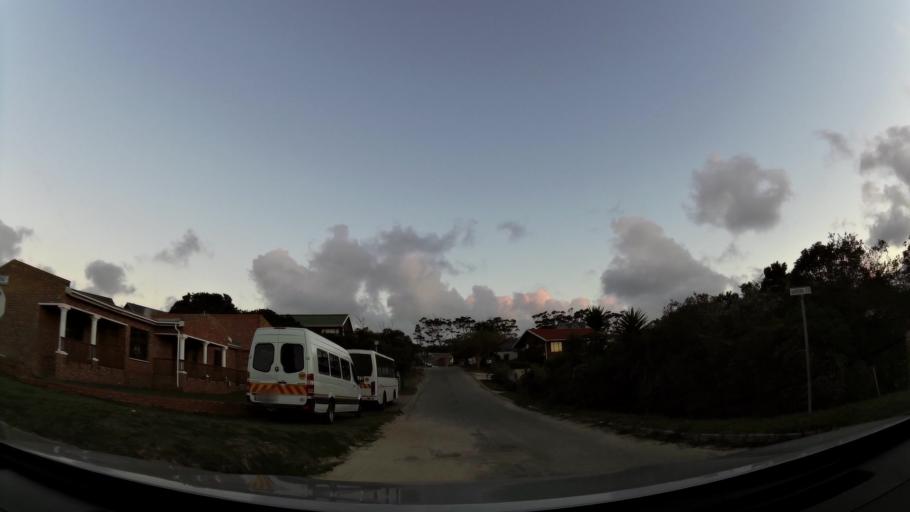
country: ZA
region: Western Cape
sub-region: Eden District Municipality
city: Knysna
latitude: -34.0274
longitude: 22.8097
